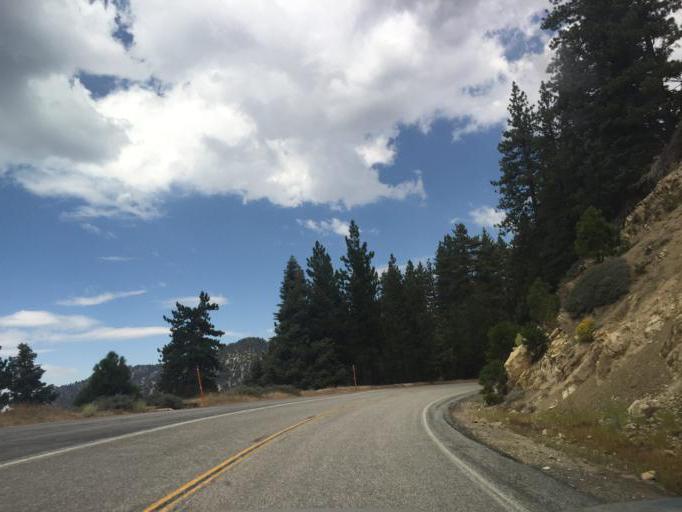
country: US
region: California
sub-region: Los Angeles County
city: Littlerock
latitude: 34.3519
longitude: -117.8898
